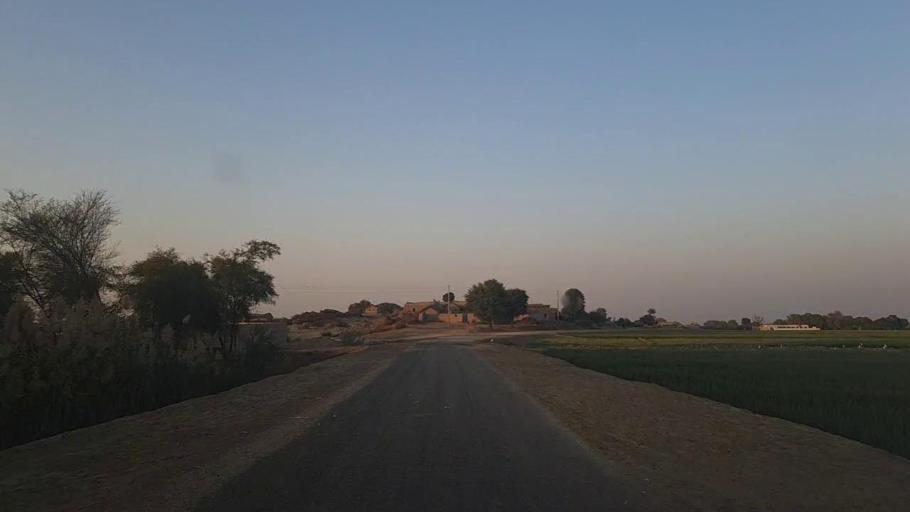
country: PK
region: Sindh
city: Jam Sahib
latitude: 26.3674
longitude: 68.7218
